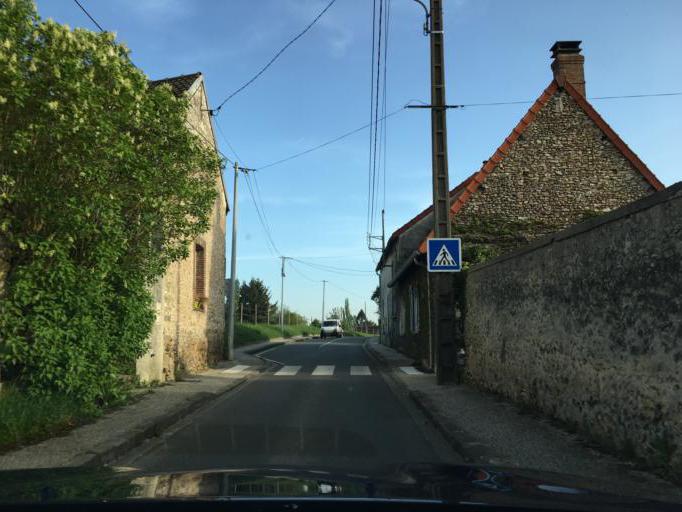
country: FR
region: Centre
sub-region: Departement d'Eure-et-Loir
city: Epernon
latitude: 48.6329
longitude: 1.6805
